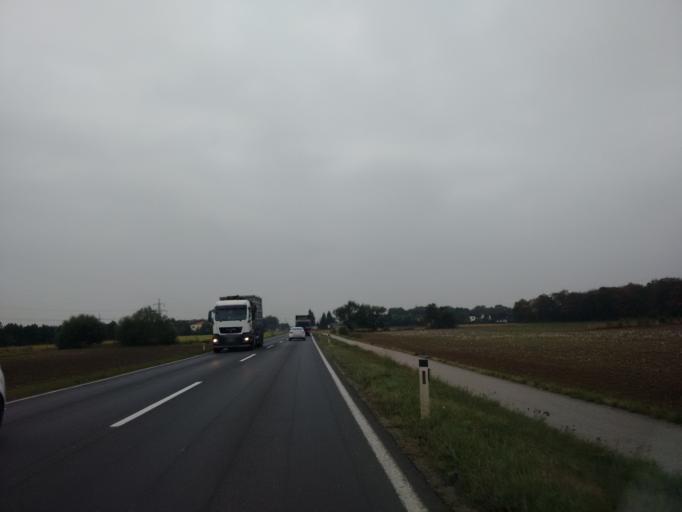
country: AT
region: Upper Austria
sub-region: Politischer Bezirk Linz-Land
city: Horsching
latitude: 48.2106
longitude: 14.1735
